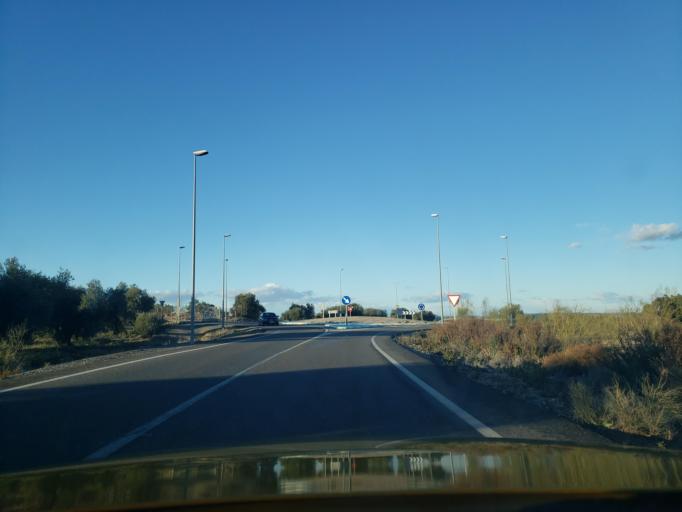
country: ES
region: Castille-La Mancha
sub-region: Province of Toledo
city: Toledo
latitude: 39.8358
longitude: -4.0196
